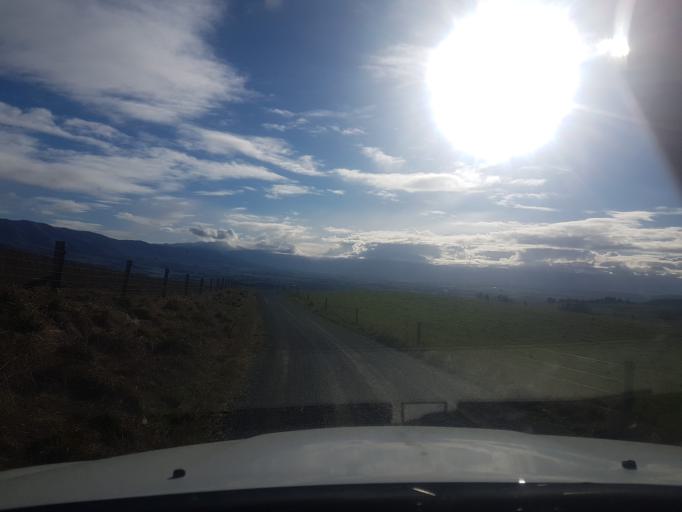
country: NZ
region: Canterbury
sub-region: Timaru District
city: Pleasant Point
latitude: -44.1741
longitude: 170.8898
